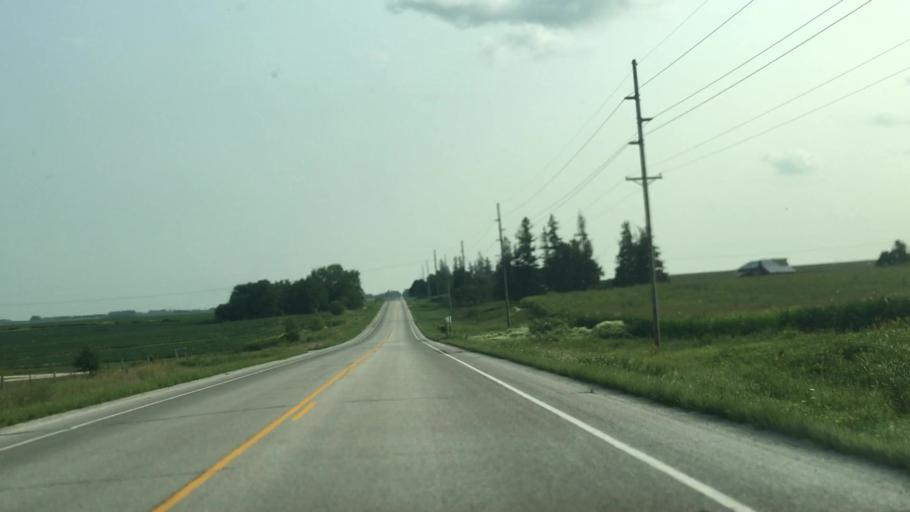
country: US
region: Minnesota
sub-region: Fillmore County
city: Harmony
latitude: 43.5545
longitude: -91.9297
